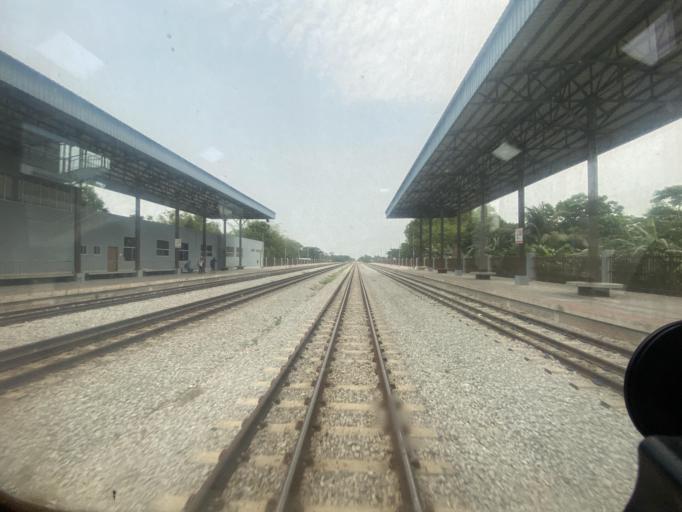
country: BD
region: Chittagong
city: Laksham
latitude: 23.3060
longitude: 91.1383
